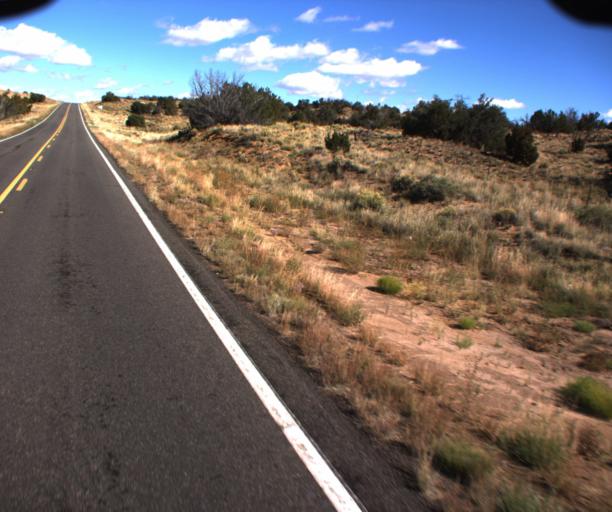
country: US
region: Arizona
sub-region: Apache County
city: Saint Johns
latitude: 34.8179
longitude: -109.2375
